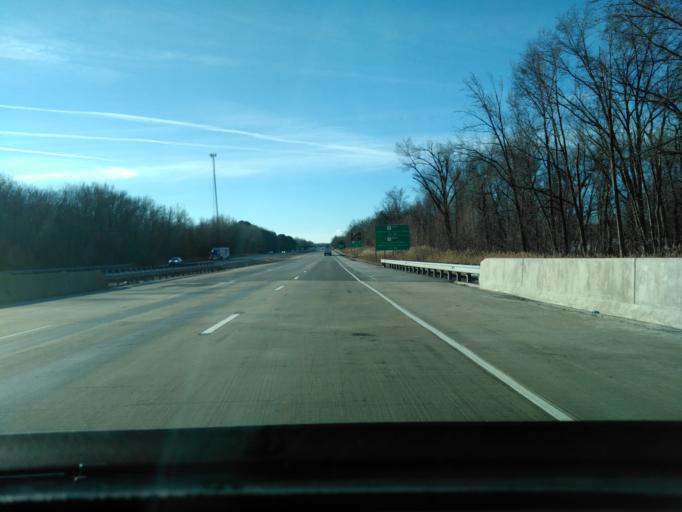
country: US
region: Illinois
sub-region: Williamson County
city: Johnston City
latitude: 37.7998
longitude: -88.9461
